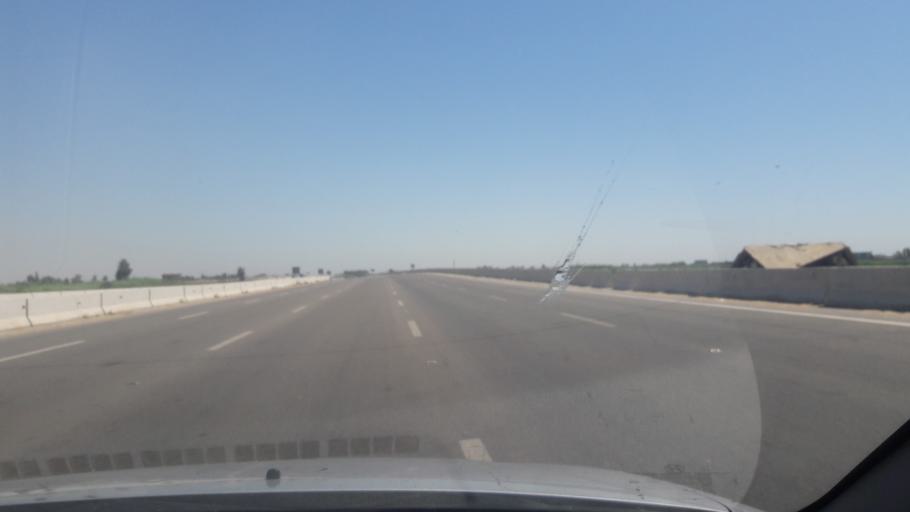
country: EG
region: Muhafazat Bur Sa`id
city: Port Said
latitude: 31.0900
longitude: 32.2328
